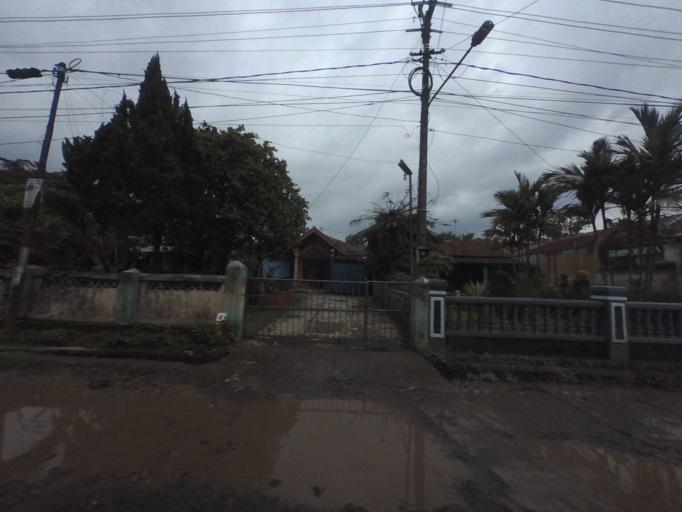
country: ID
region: West Java
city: Cicurug
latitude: -6.8381
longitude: 106.7607
